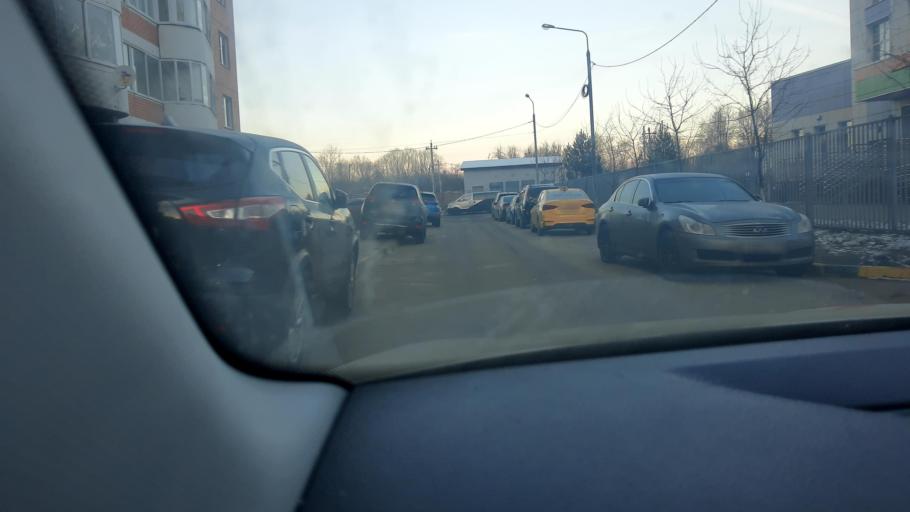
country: RU
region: Moskovskaya
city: Shcherbinka
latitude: 55.5275
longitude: 37.5896
